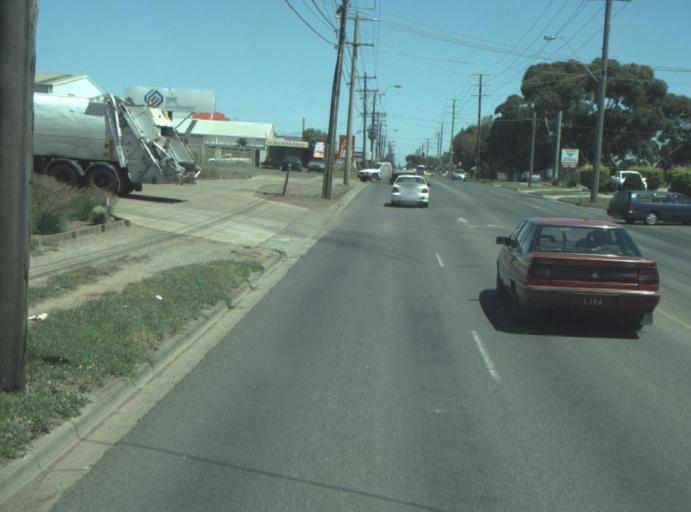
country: AU
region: Victoria
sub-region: Greater Geelong
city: Bell Park
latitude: -38.1080
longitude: 144.3440
